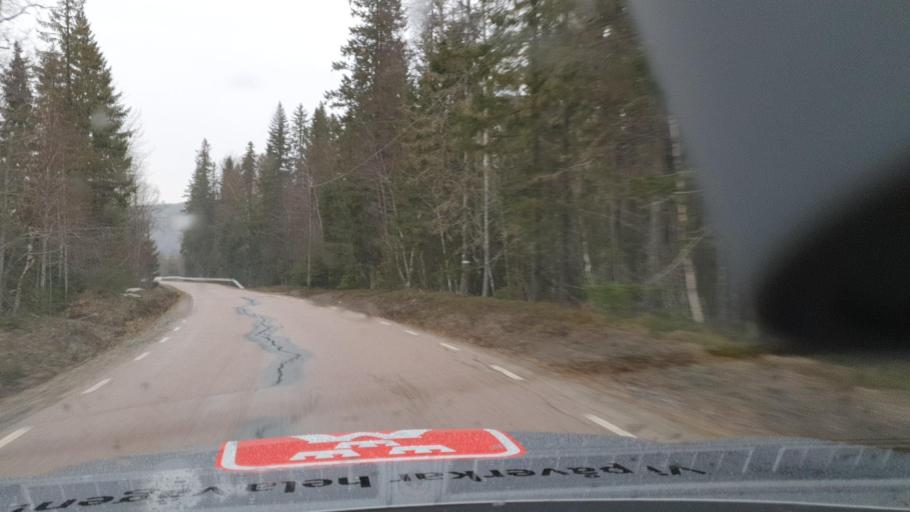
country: SE
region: Vaesternorrland
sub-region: OErnskoeldsviks Kommun
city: Bjasta
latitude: 63.2060
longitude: 18.4199
